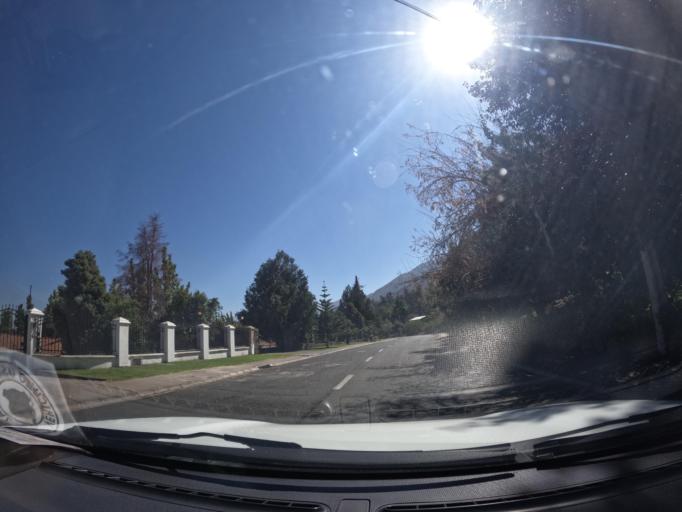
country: CL
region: Santiago Metropolitan
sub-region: Provincia de Santiago
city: Villa Presidente Frei, Nunoa, Santiago, Chile
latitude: -33.4736
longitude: -70.5212
